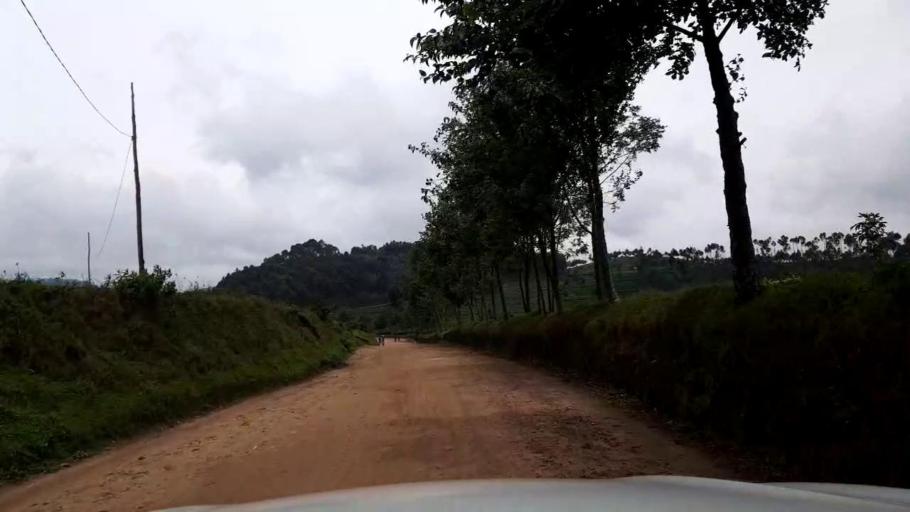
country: RW
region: Western Province
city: Kibuye
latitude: -1.9539
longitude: 29.4060
